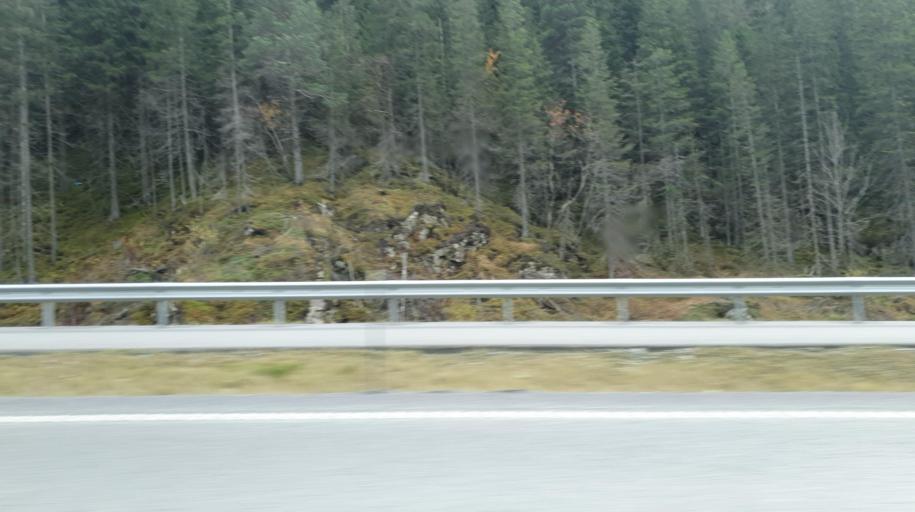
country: NO
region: Sor-Trondelag
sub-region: Klaebu
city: Klaebu
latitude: 63.3177
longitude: 10.3897
